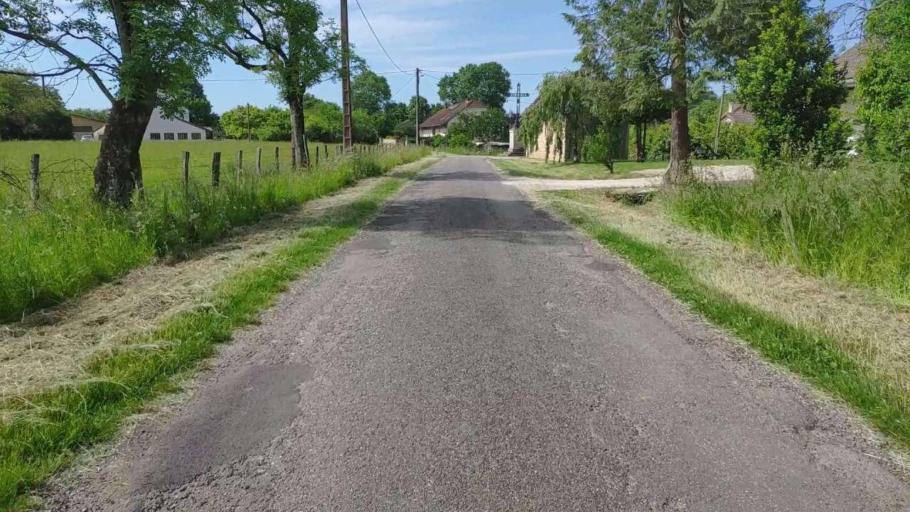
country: FR
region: Franche-Comte
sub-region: Departement du Jura
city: Bletterans
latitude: 46.7090
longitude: 5.4564
